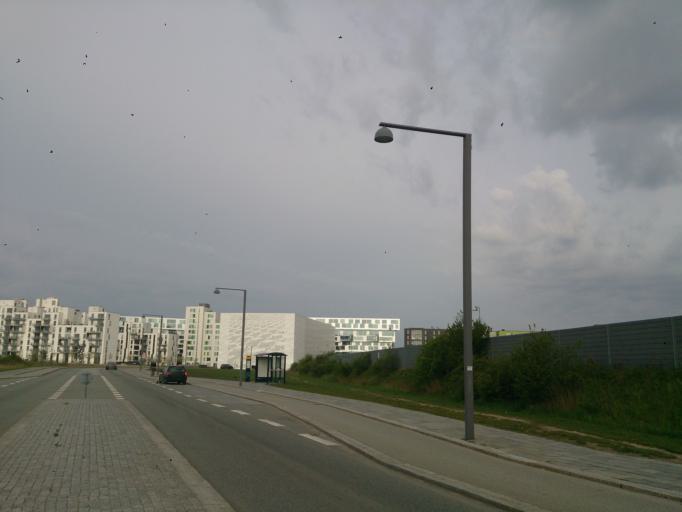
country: DK
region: Capital Region
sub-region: Tarnby Kommune
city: Tarnby
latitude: 55.6181
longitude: 12.5785
